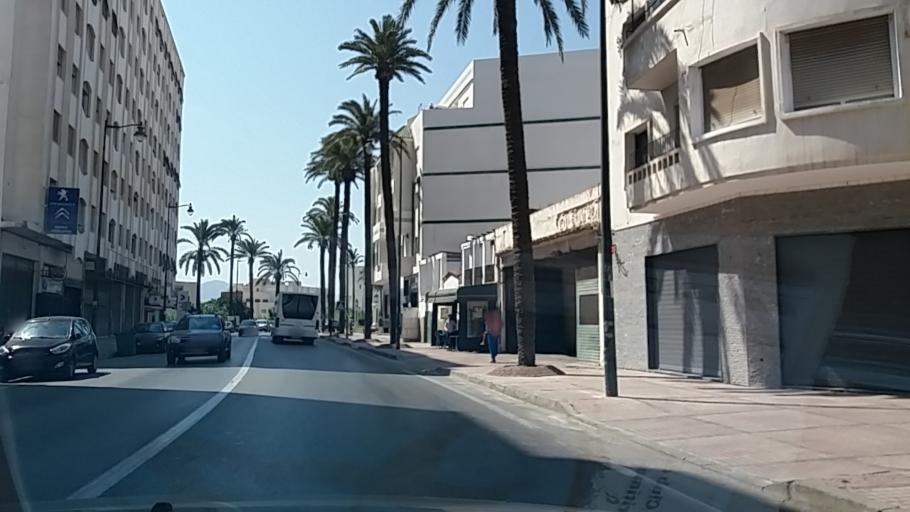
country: MA
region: Tanger-Tetouan
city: Tetouan
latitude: 35.5684
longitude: -5.3766
